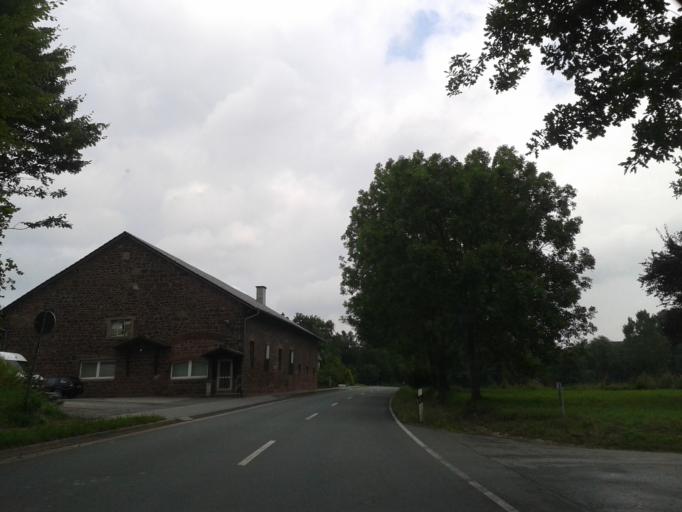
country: DE
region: North Rhine-Westphalia
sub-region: Regierungsbezirk Detmold
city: Blomberg
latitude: 51.9426
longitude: 9.0845
